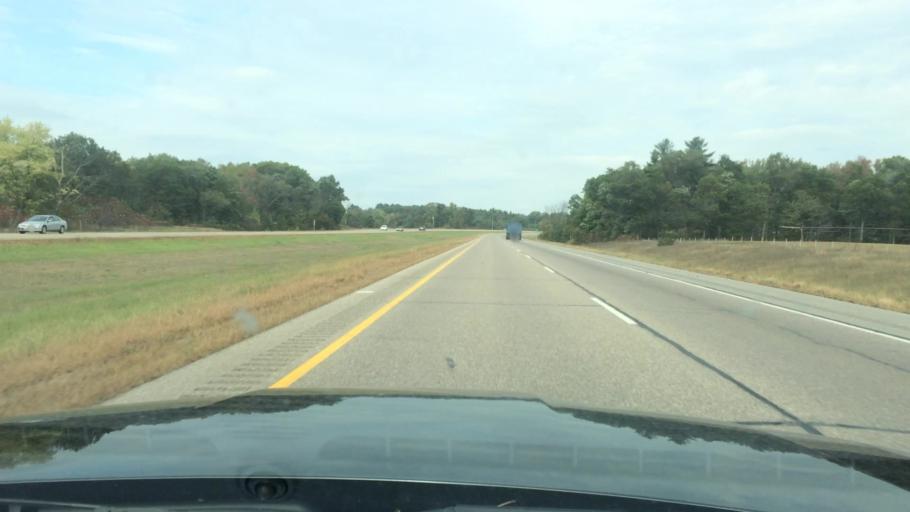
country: US
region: Wisconsin
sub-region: Portage County
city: Stevens Point
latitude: 44.6571
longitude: -89.6412
